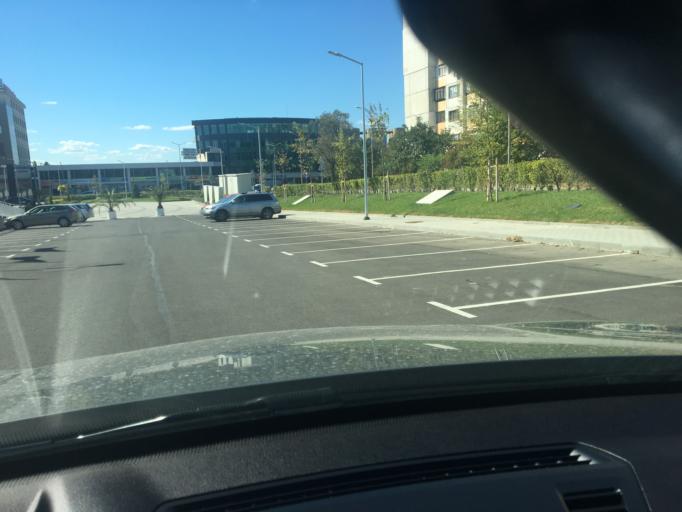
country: BG
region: Burgas
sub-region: Obshtina Burgas
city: Burgas
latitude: 42.5133
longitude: 27.4585
